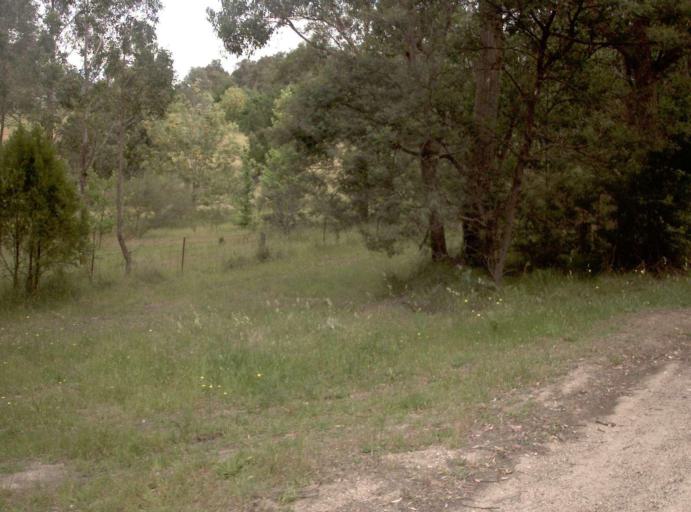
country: AU
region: Victoria
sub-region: East Gippsland
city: Bairnsdale
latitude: -37.7434
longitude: 147.5987
